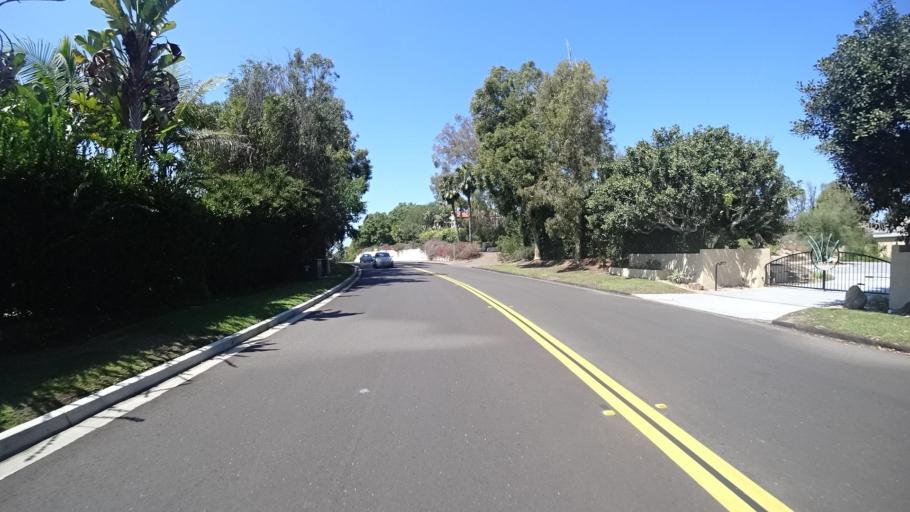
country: US
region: California
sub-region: San Diego County
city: Fairbanks Ranch
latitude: 32.9833
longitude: -117.1899
